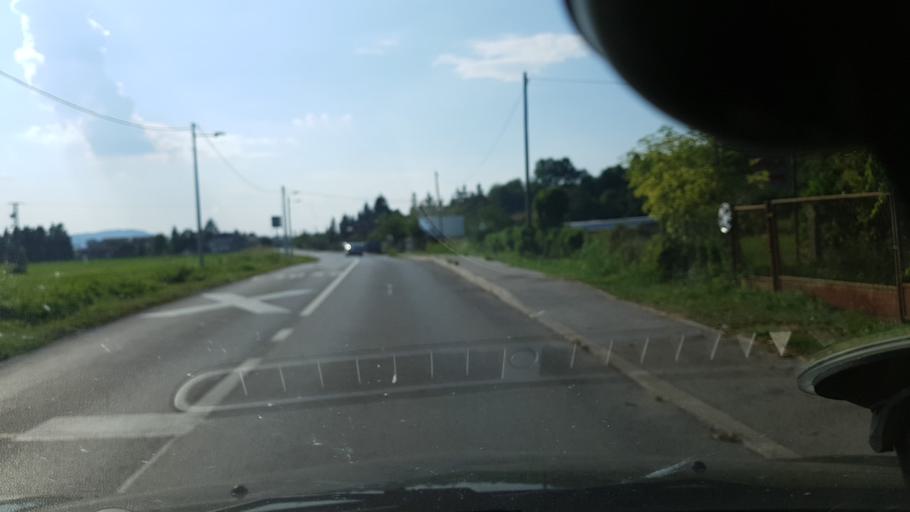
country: HR
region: Zagrebacka
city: Bregana
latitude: 45.8848
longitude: 15.7080
